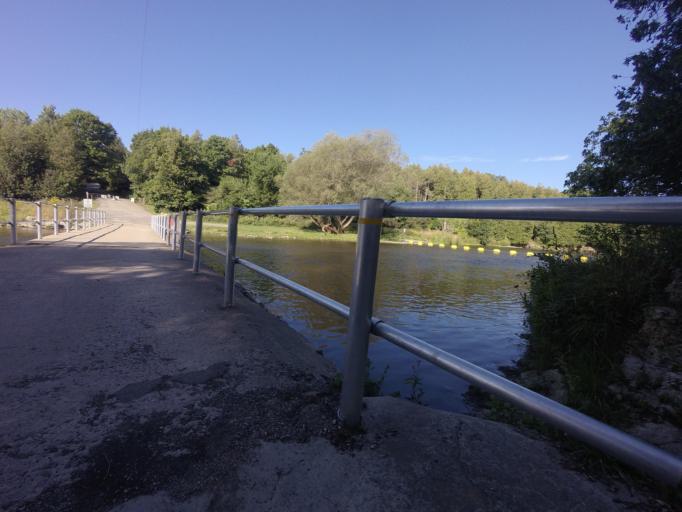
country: CA
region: Ontario
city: Waterloo
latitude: 43.6630
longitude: -80.4511
